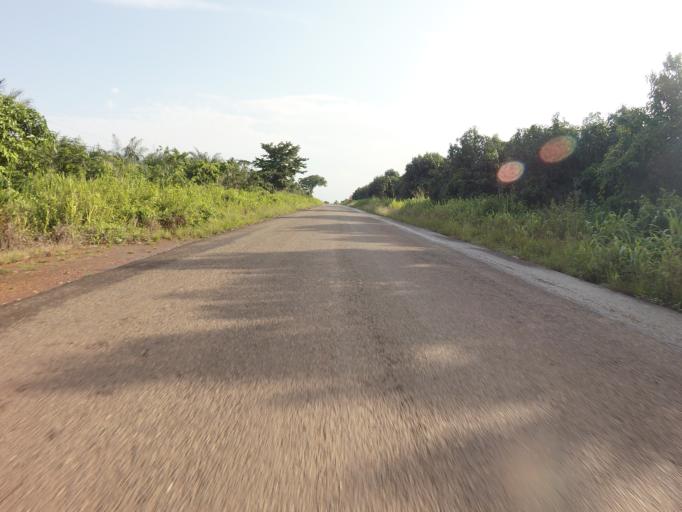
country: GH
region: Volta
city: Hohoe
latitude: 7.0803
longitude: 0.4410
